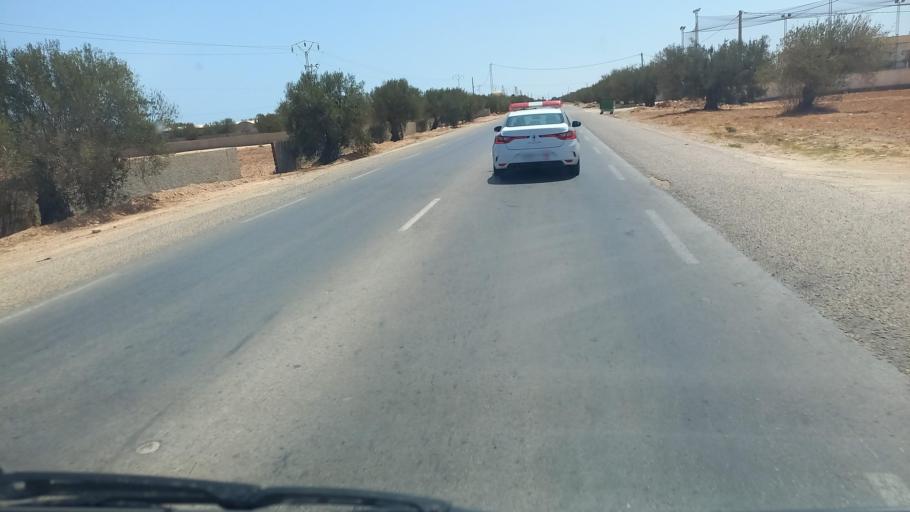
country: TN
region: Madanin
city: Zarzis
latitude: 33.5468
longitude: 11.0710
